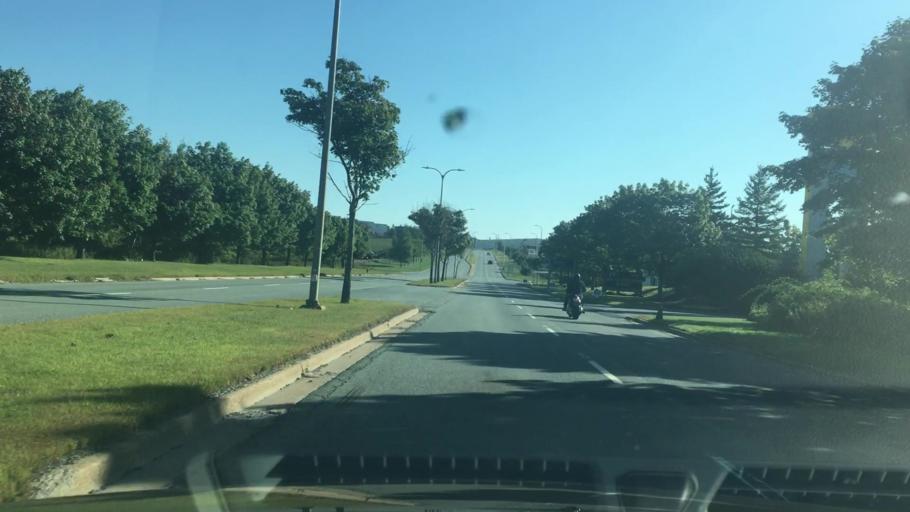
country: CA
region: Nova Scotia
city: Dartmouth
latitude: 44.7154
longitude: -63.5886
